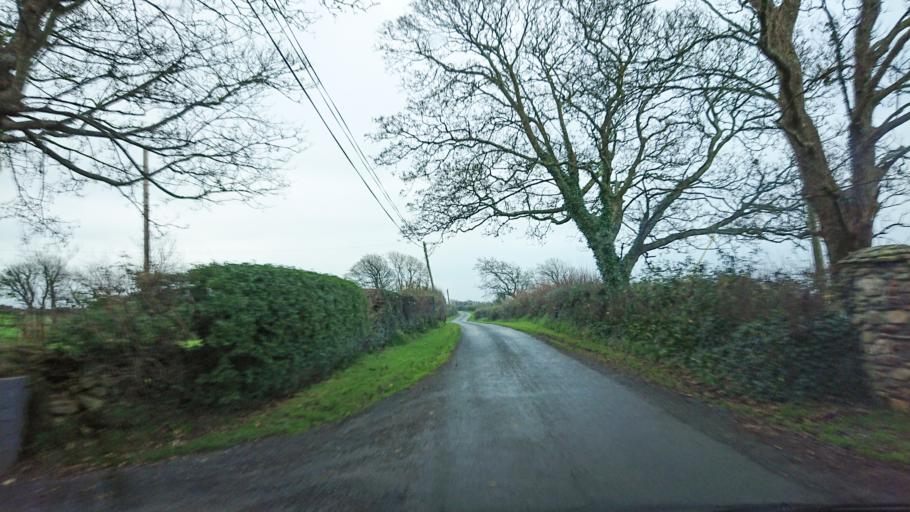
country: IE
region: Munster
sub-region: Waterford
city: Dunmore East
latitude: 52.2049
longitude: -6.9954
